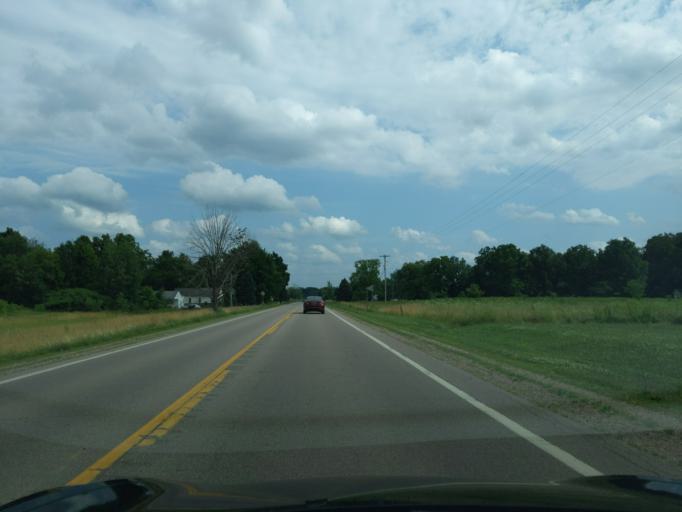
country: US
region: Michigan
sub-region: Eaton County
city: Eaton Rapids
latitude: 42.4562
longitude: -84.6539
